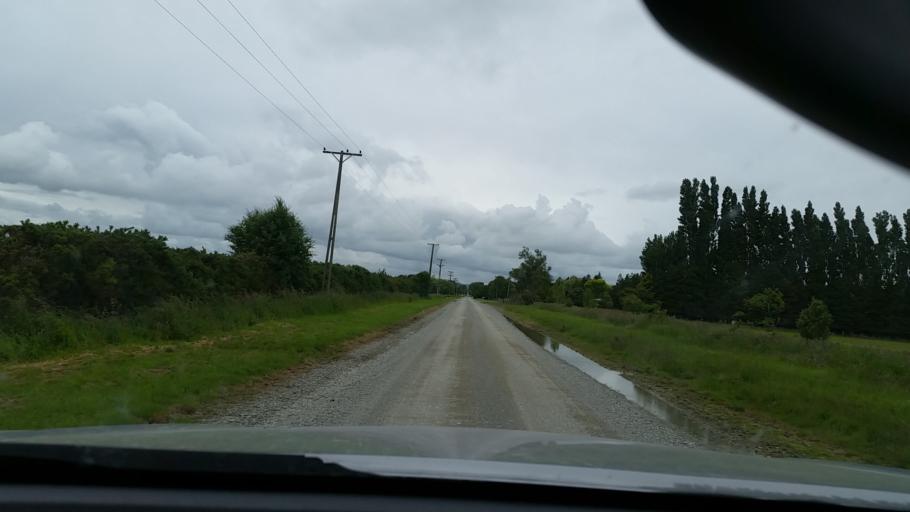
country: NZ
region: Southland
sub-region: Southland District
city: Winton
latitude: -46.1837
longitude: 168.2951
